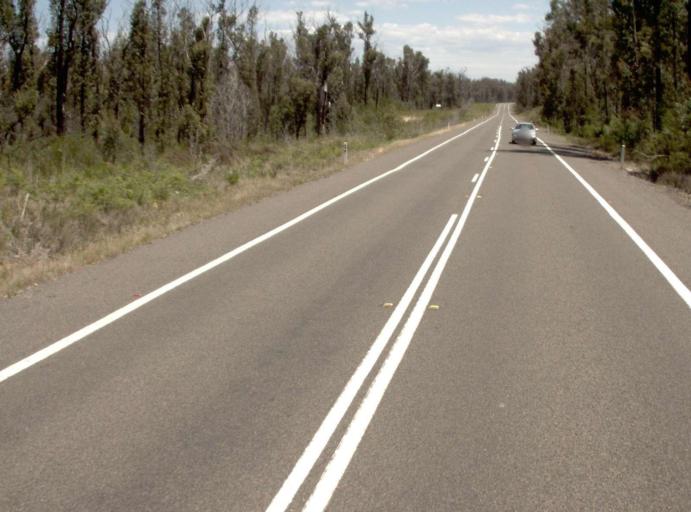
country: AU
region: Victoria
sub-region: East Gippsland
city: Lakes Entrance
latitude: -37.7491
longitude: 148.2231
